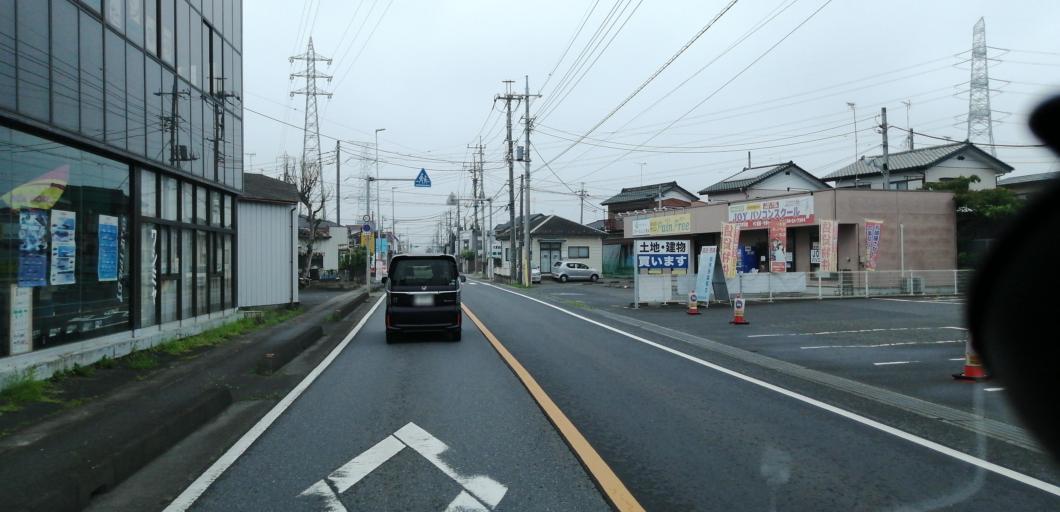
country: JP
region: Saitama
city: Kukichuo
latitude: 36.1016
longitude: 139.6646
